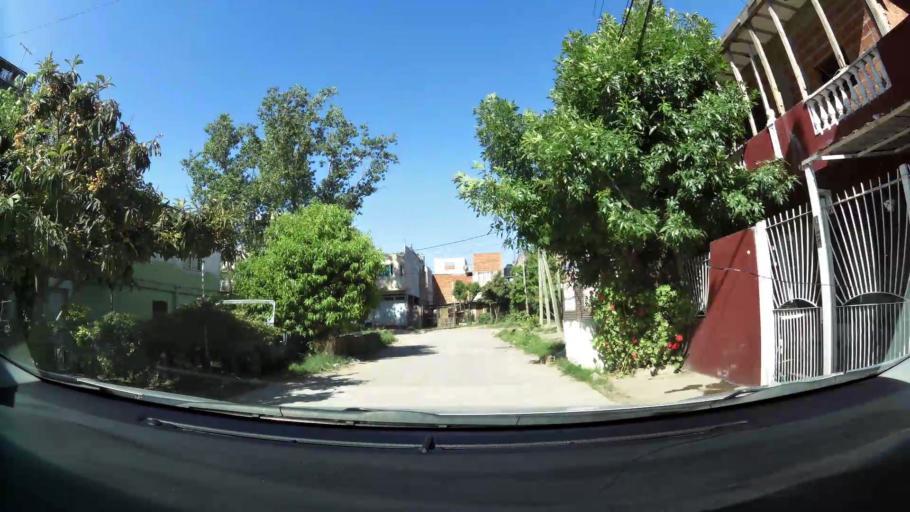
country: AR
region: Buenos Aires F.D.
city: Villa Lugano
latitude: -34.7083
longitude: -58.4760
